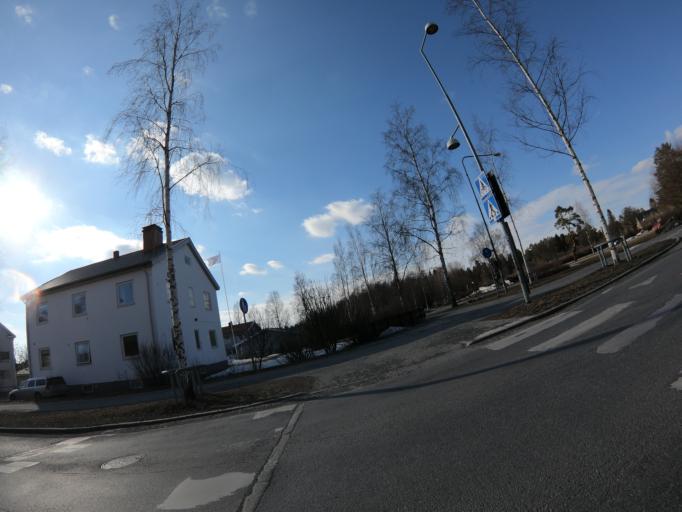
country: SE
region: Vaesterbotten
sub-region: Umea Kommun
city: Umea
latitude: 63.8442
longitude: 20.2896
